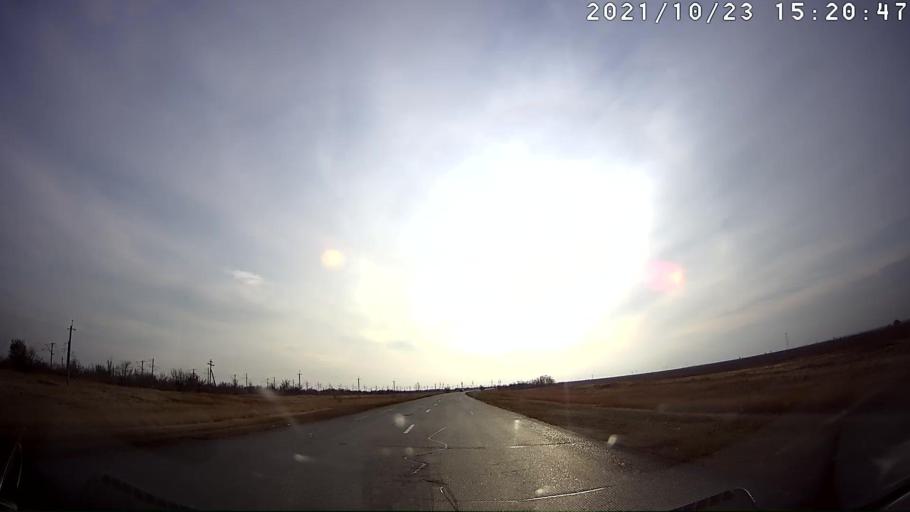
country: RU
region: Volgograd
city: Bereslavka
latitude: 48.3178
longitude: 44.3223
